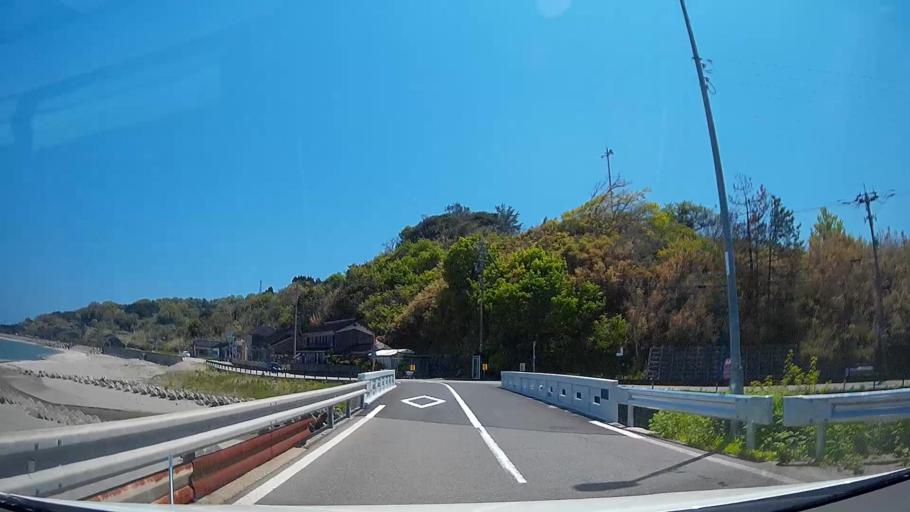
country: JP
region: Ishikawa
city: Nanao
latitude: 37.5269
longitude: 137.2822
